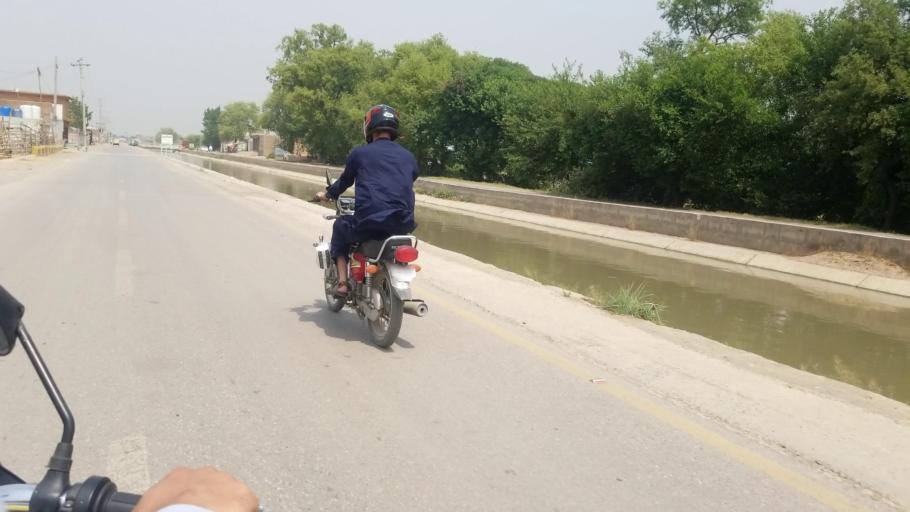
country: PK
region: Khyber Pakhtunkhwa
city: Peshawar
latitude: 33.9503
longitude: 71.5530
